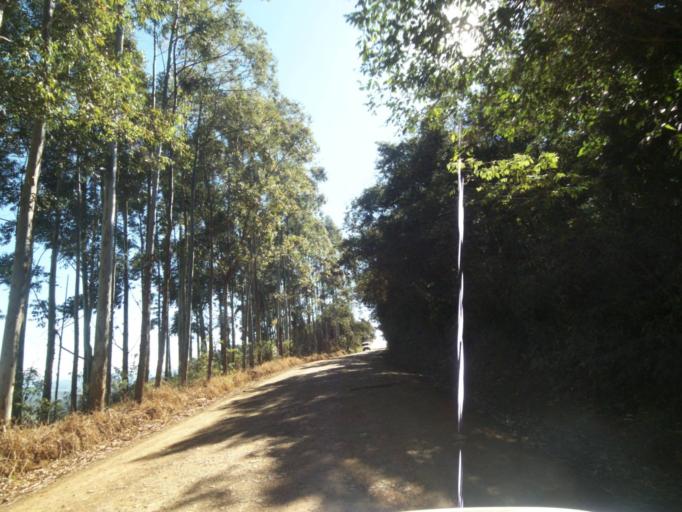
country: BR
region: Parana
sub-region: Tibagi
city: Tibagi
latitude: -24.5924
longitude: -50.6049
